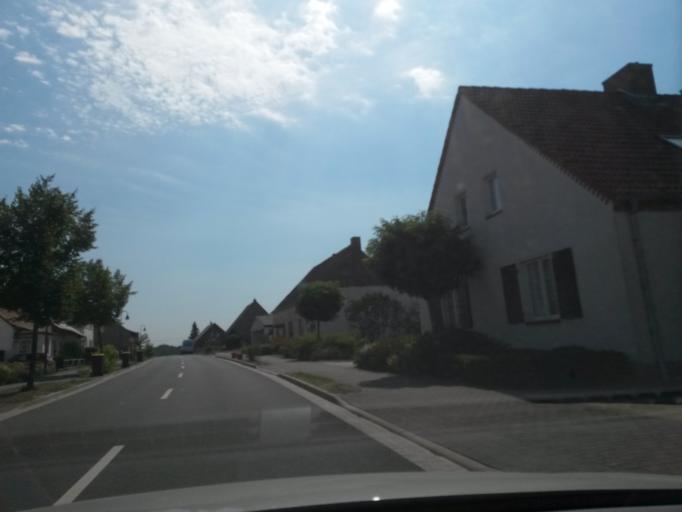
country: DE
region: Saxony-Anhalt
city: Jerichow
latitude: 52.4163
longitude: 11.9960
